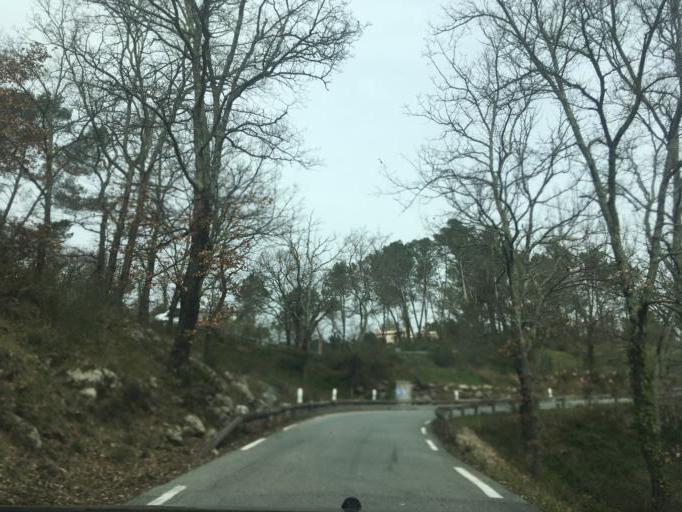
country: FR
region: Provence-Alpes-Cote d'Azur
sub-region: Departement du Var
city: Callian
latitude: 43.5887
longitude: 6.7305
